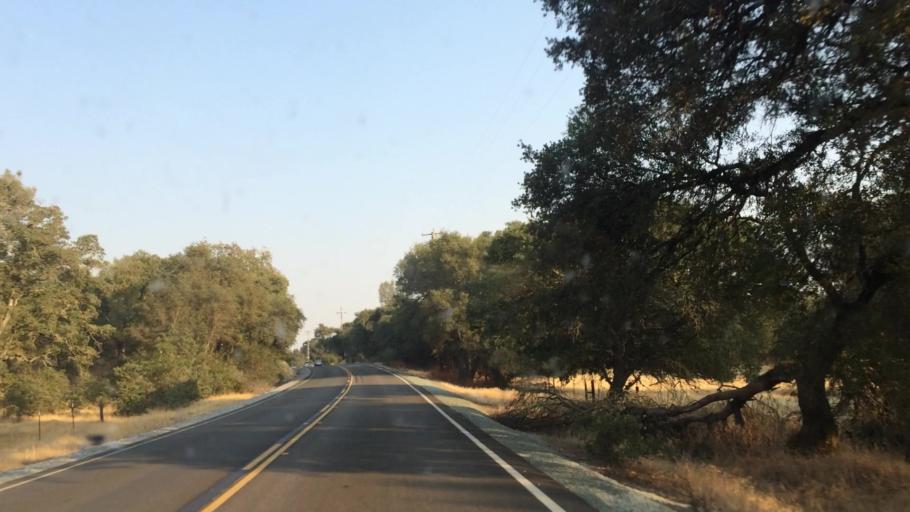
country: US
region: California
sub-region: Amador County
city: Ione
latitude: 38.3829
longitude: -120.9894
